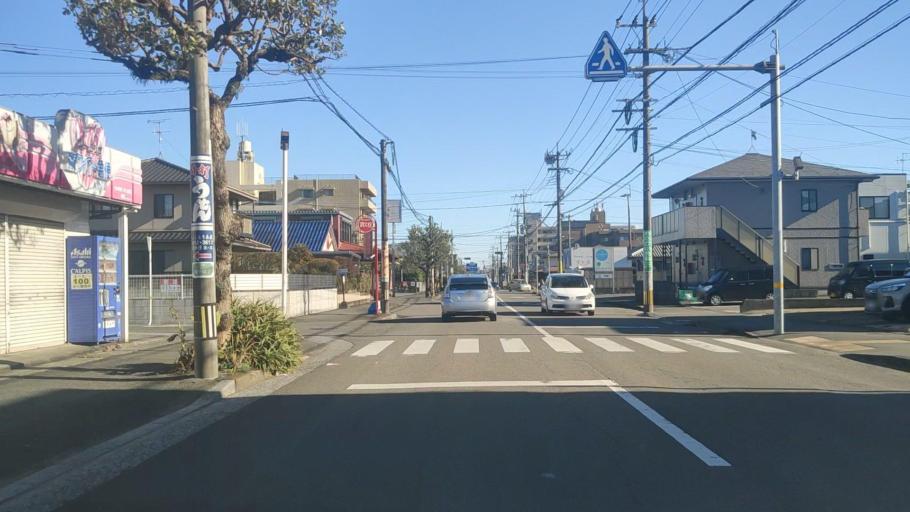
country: JP
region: Miyazaki
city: Miyazaki-shi
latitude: 31.8969
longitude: 131.4285
